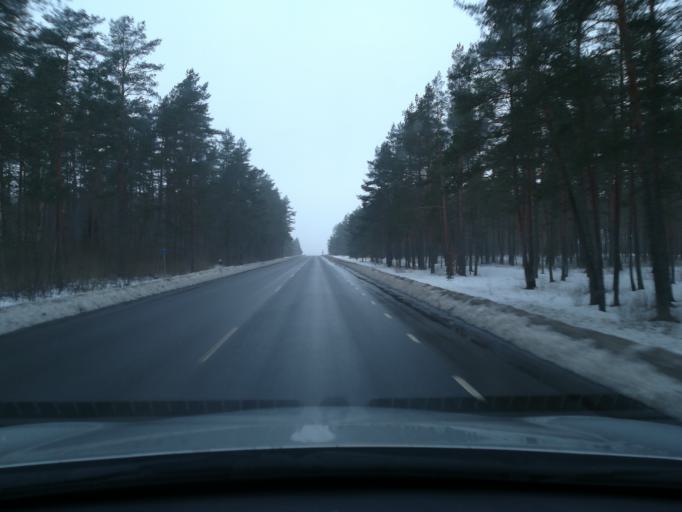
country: EE
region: Harju
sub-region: Raasiku vald
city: Arukula
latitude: 59.3604
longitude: 25.0544
